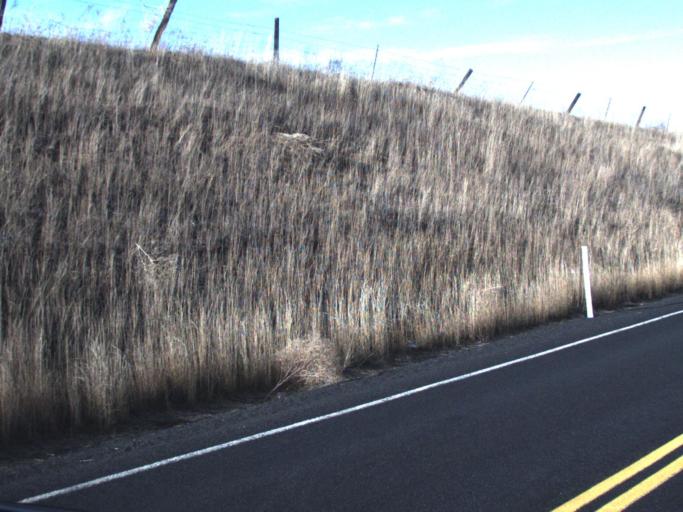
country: US
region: Washington
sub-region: Lincoln County
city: Davenport
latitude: 47.8468
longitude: -118.2134
